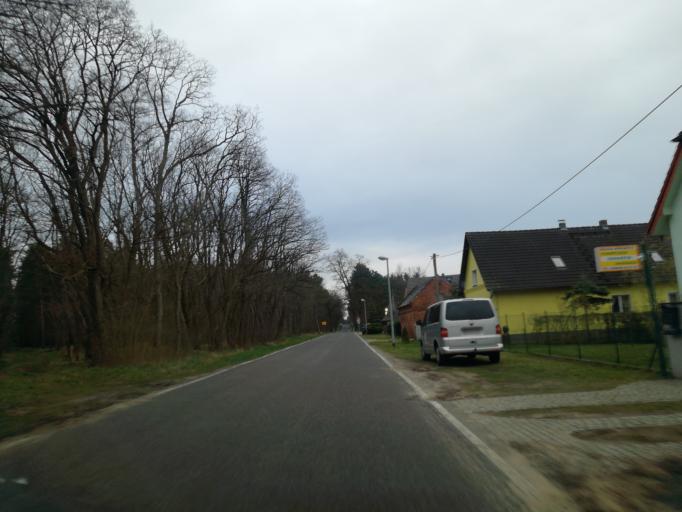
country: DE
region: Brandenburg
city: Vetschau
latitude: 51.7576
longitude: 14.1306
